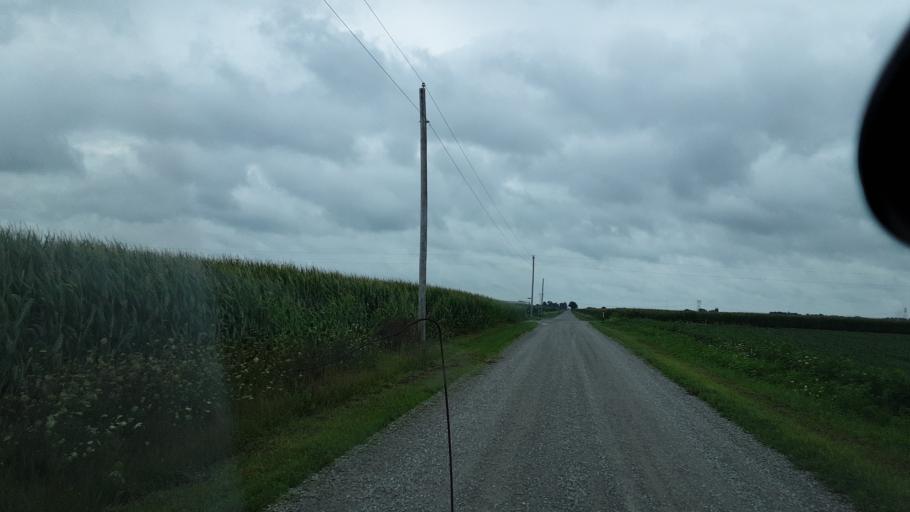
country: US
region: Indiana
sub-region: Wells County
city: Bluffton
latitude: 40.7730
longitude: -85.0713
